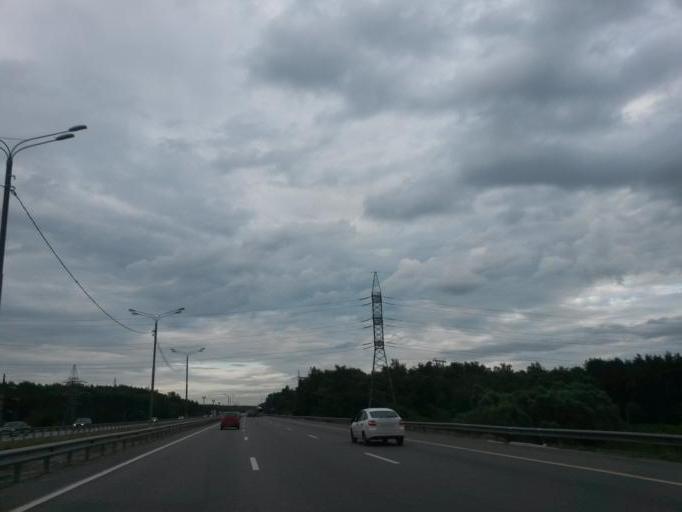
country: RU
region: Moskovskaya
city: Domodedovo
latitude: 55.4587
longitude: 37.7721
